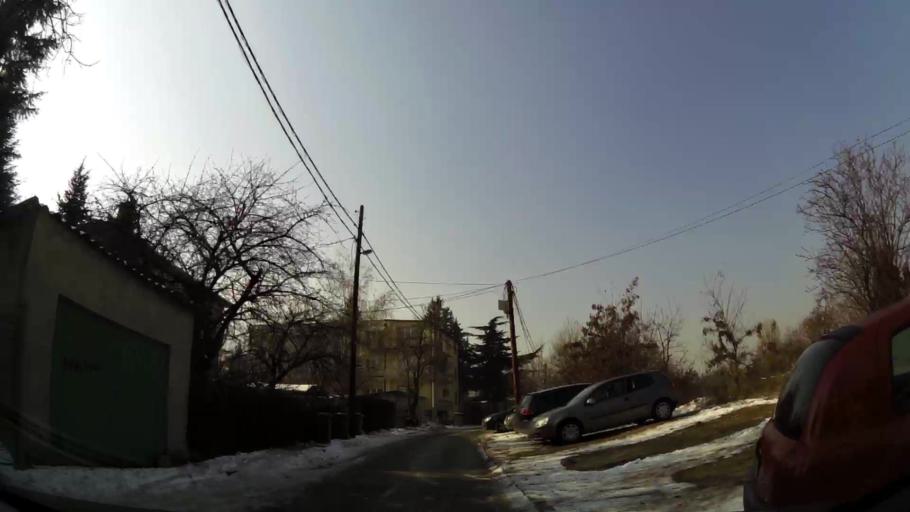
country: MK
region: Karpos
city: Skopje
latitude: 41.9858
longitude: 21.4299
